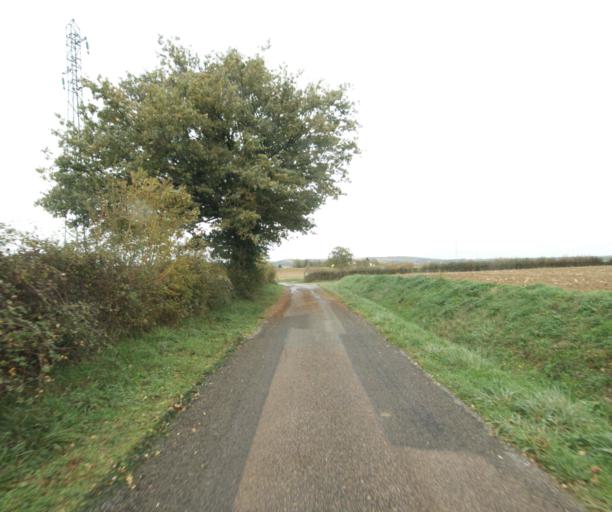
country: FR
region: Rhone-Alpes
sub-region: Departement de l'Ain
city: Pont-de-Vaux
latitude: 46.4670
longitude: 4.8724
